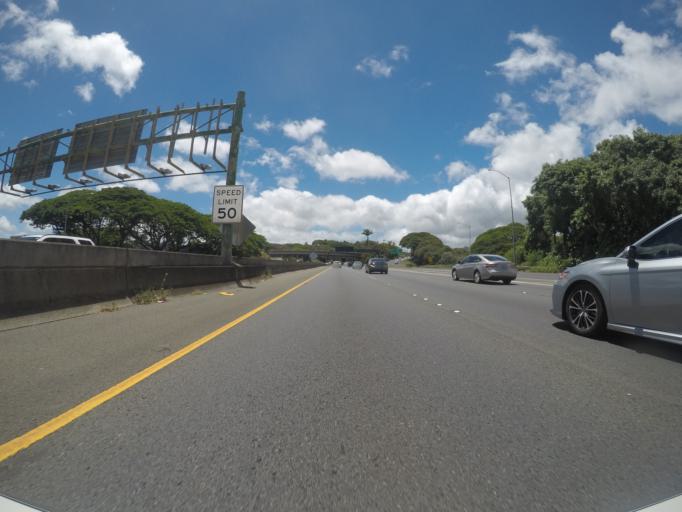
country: US
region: Hawaii
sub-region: Honolulu County
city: Halawa Heights
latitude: 21.3465
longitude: -157.8941
